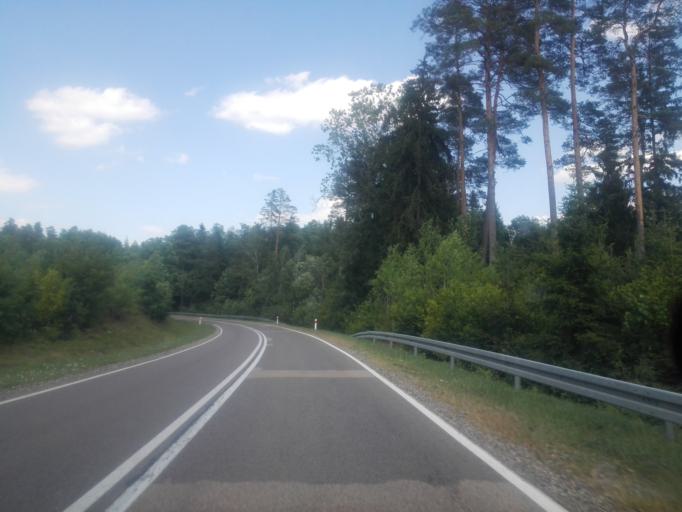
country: PL
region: Podlasie
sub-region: Powiat sejnenski
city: Sejny
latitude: 54.0109
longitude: 23.3291
